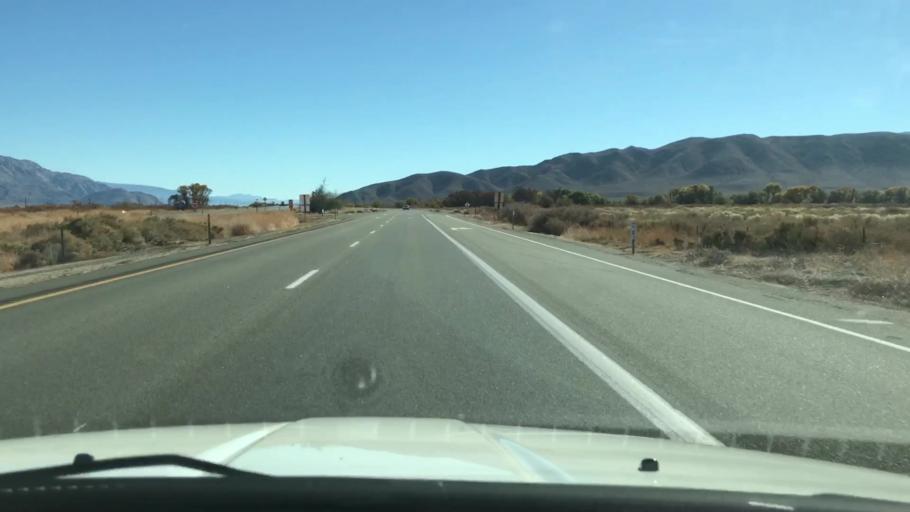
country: US
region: California
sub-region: Inyo County
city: Lone Pine
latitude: 36.7100
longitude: -118.1322
